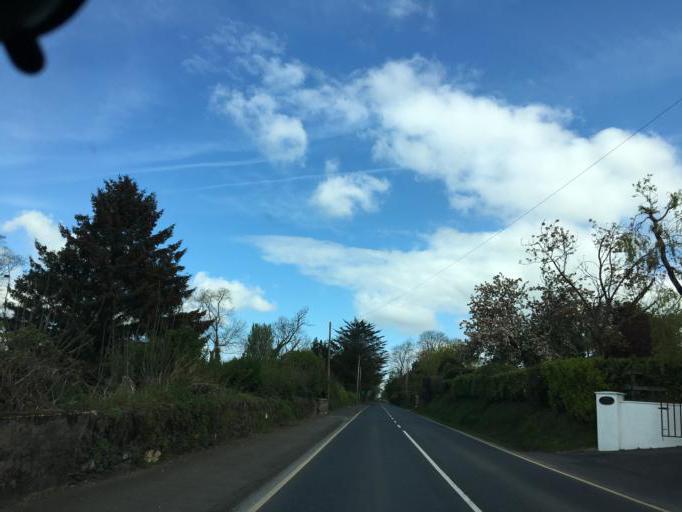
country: IE
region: Leinster
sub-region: Loch Garman
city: New Ross
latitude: 52.4105
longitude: -6.9380
